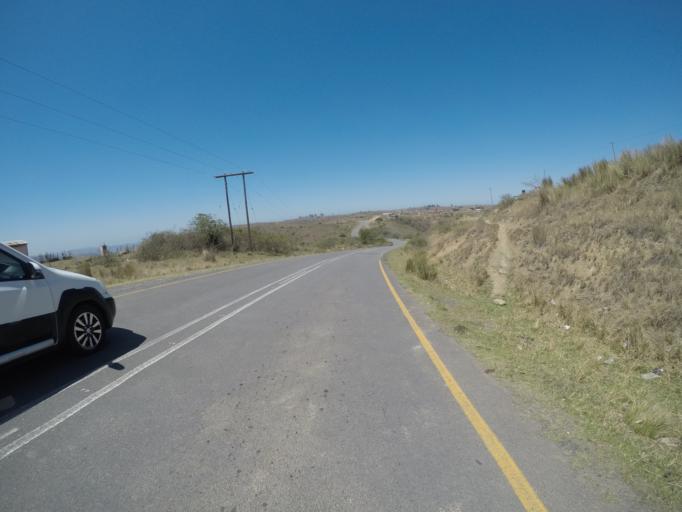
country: ZA
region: Eastern Cape
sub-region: OR Tambo District Municipality
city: Mthatha
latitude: -31.9091
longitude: 28.9516
